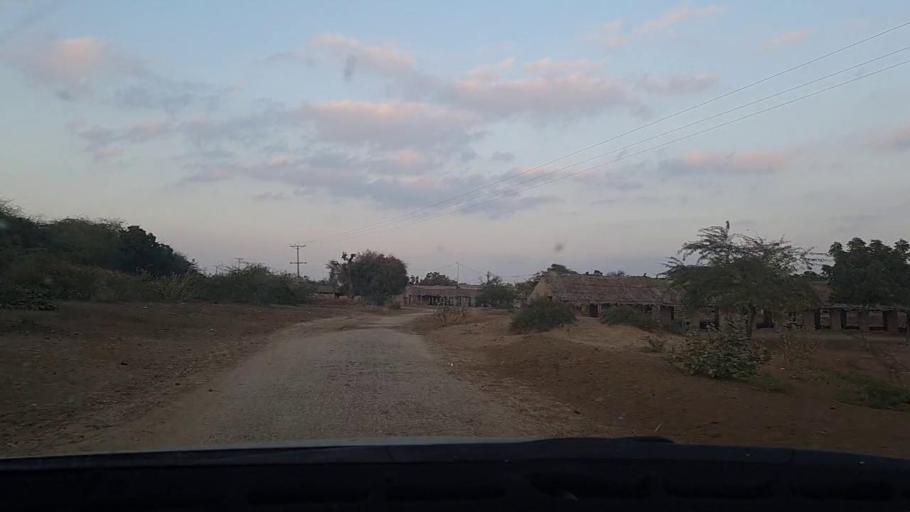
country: PK
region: Sindh
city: Tando Mittha Khan
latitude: 25.9537
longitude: 69.3421
